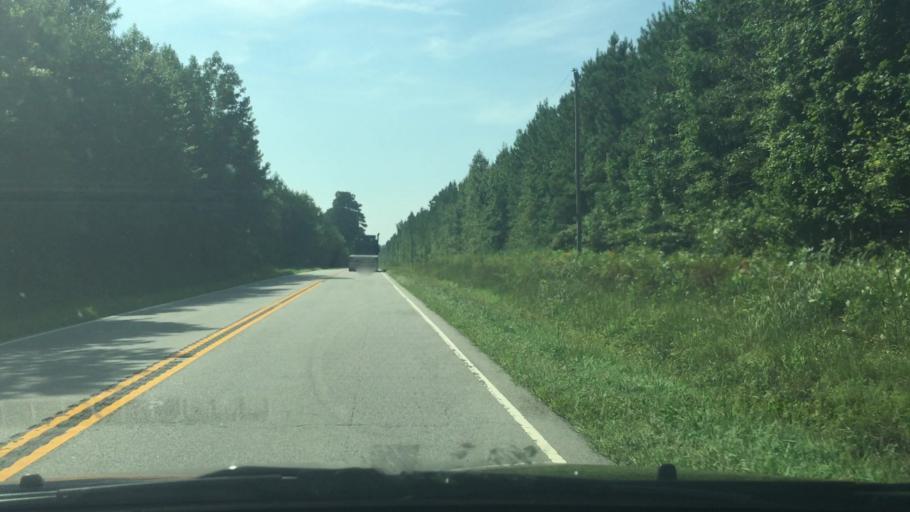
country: US
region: Virginia
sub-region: Sussex County
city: Sussex
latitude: 36.8674
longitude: -77.1413
